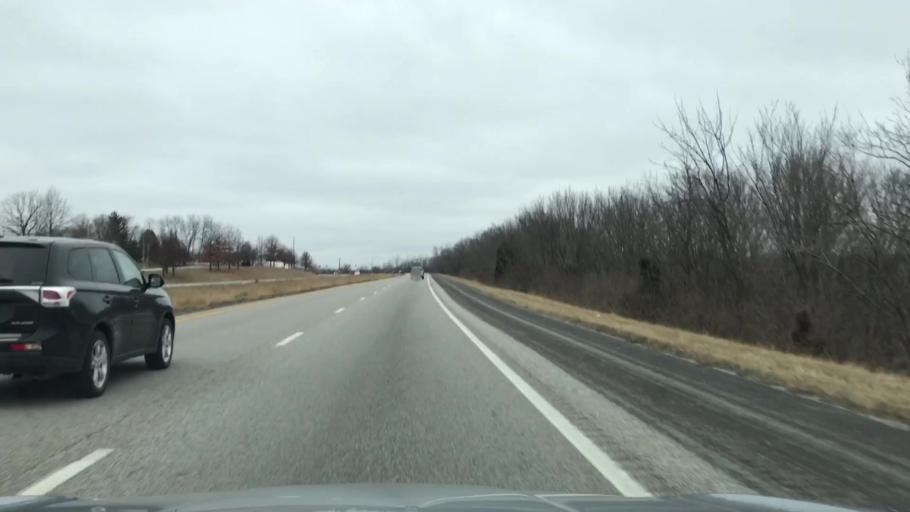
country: US
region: Missouri
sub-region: Clay County
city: Liberty
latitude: 39.2256
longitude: -94.4117
